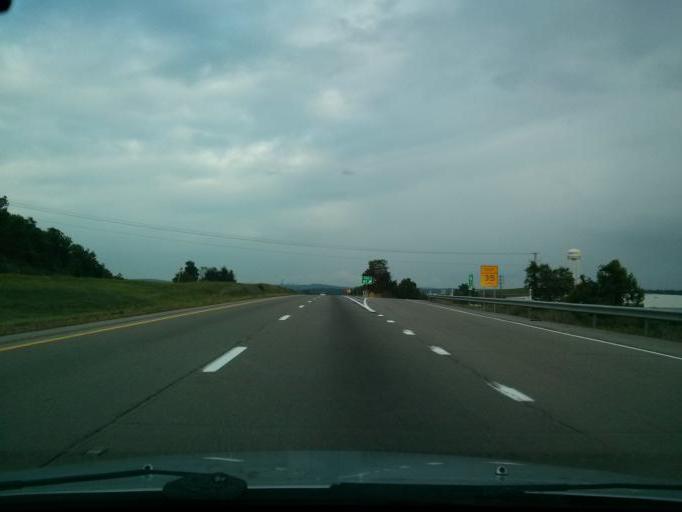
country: US
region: Pennsylvania
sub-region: Jefferson County
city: Brookville
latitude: 41.1687
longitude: -79.0500
